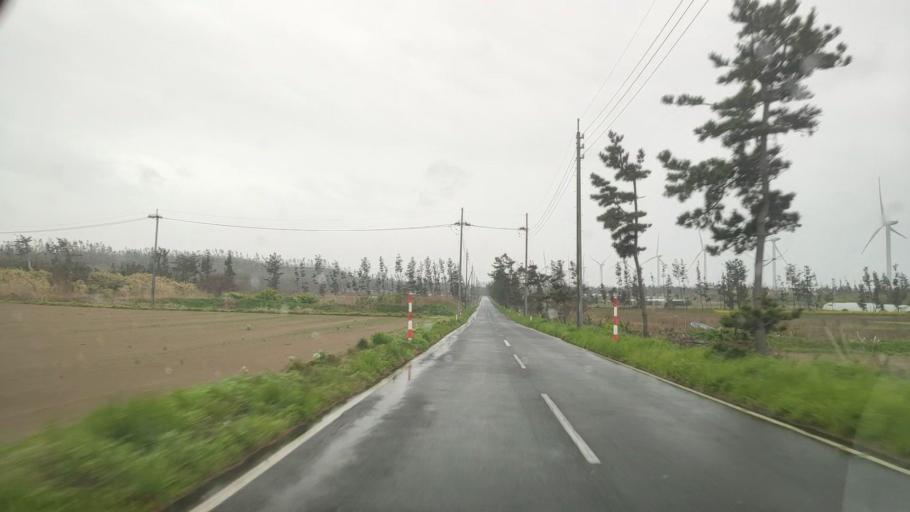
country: JP
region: Akita
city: Noshiromachi
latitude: 40.0873
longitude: 139.9593
